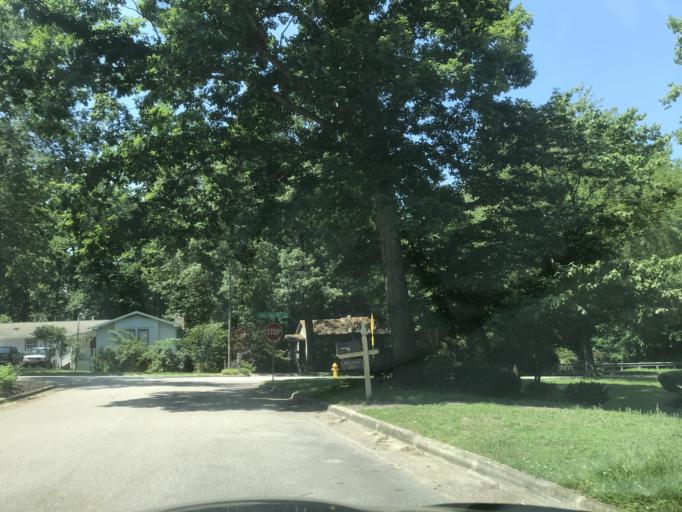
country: US
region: North Carolina
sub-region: Wake County
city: West Raleigh
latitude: 35.8631
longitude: -78.6126
